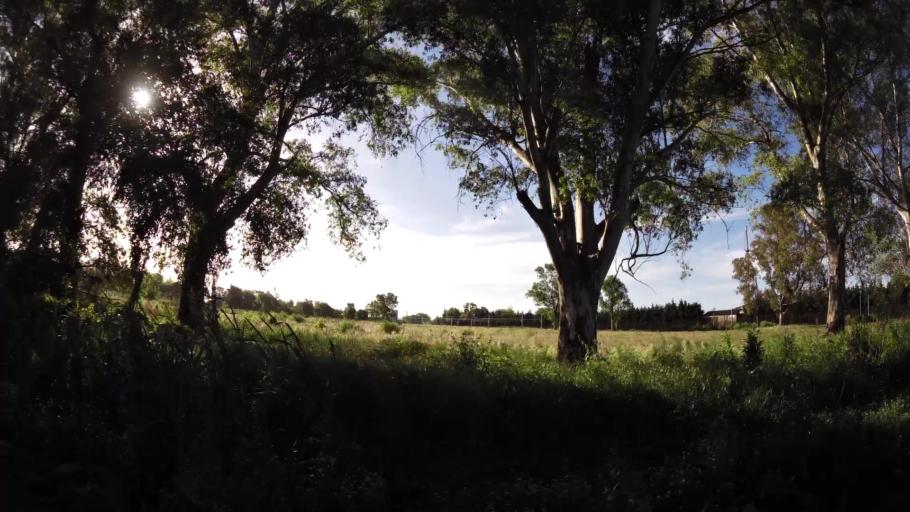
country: AR
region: Buenos Aires
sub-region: Partido de Quilmes
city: Quilmes
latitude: -34.8232
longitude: -58.2225
